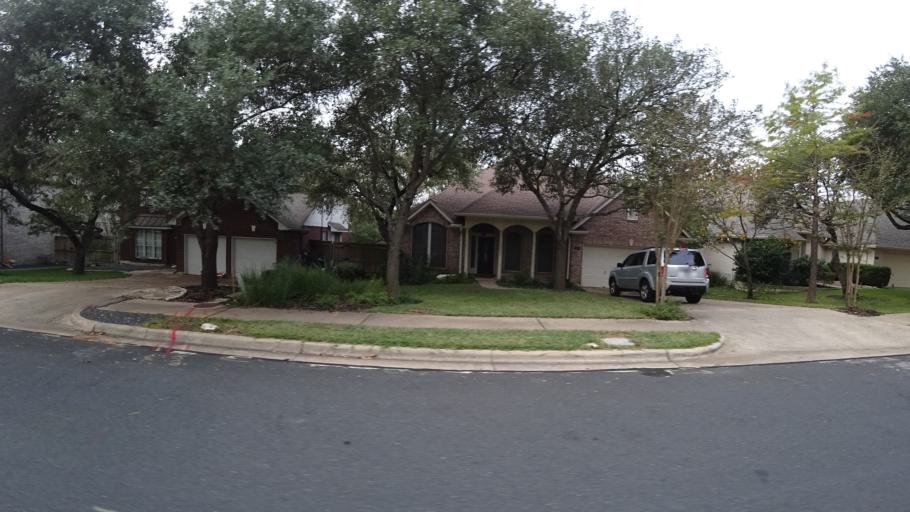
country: US
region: Texas
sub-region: Travis County
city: Shady Hollow
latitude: 30.1869
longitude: -97.8962
